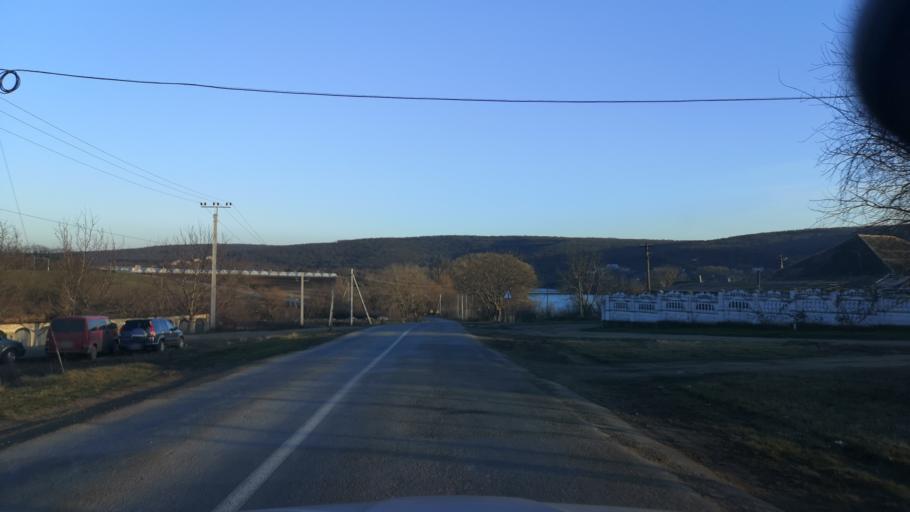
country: MD
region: Orhei
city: Orhei
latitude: 47.2866
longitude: 28.8706
